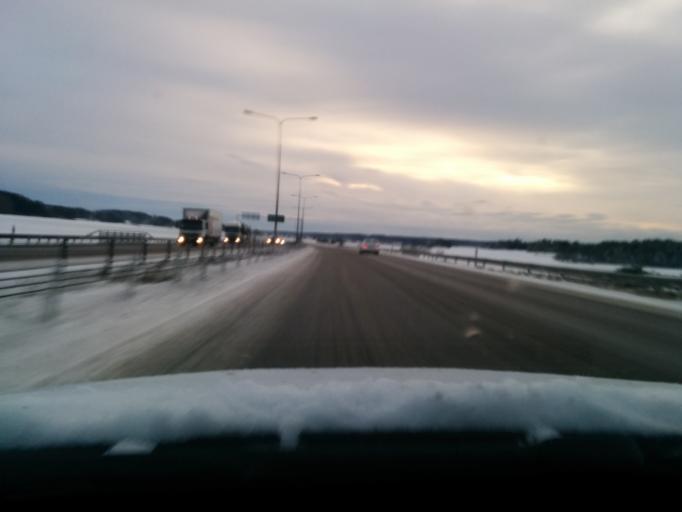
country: SE
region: Uppsala
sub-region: Uppsala Kommun
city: Saevja
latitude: 59.8294
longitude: 17.7376
